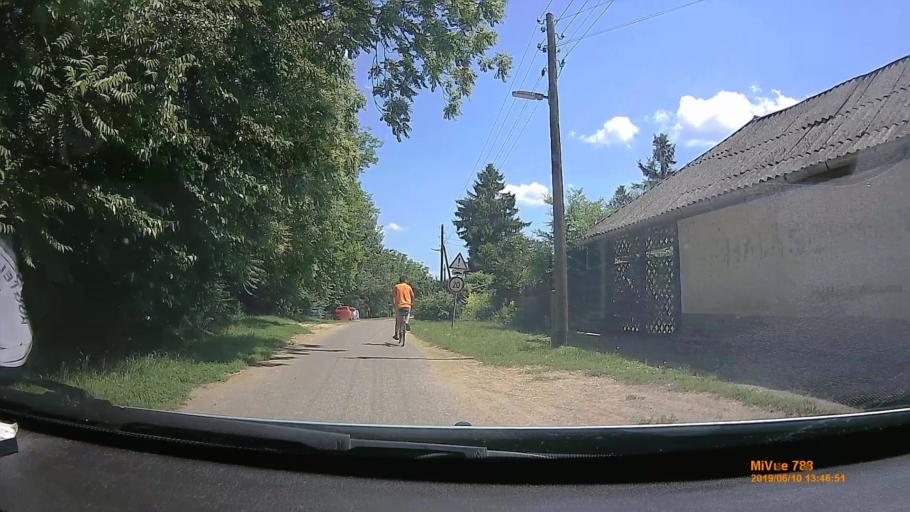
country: HU
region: Szabolcs-Szatmar-Bereg
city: Tiszadob
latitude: 48.0080
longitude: 21.1725
